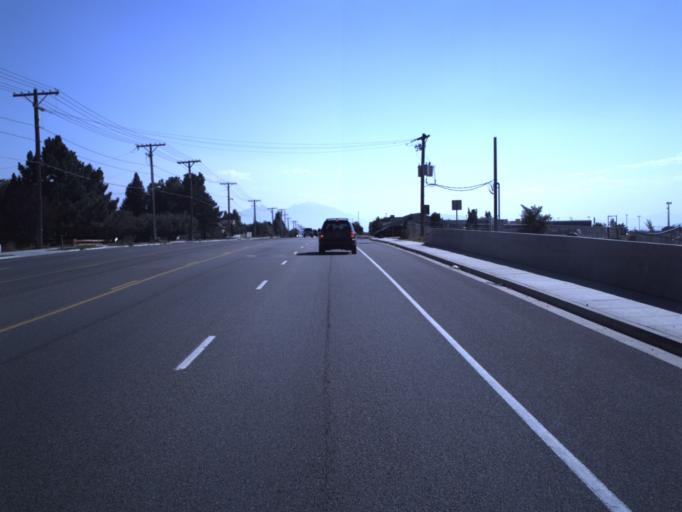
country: US
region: Utah
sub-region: Utah County
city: Cedar Hills
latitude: 40.4234
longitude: -111.7736
